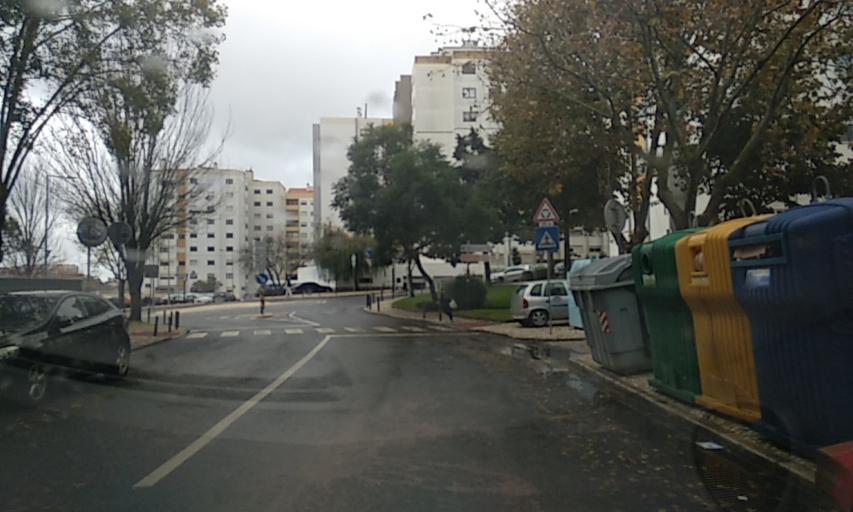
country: PT
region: Lisbon
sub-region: Sintra
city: Cacem
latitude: 38.7547
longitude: -9.2860
